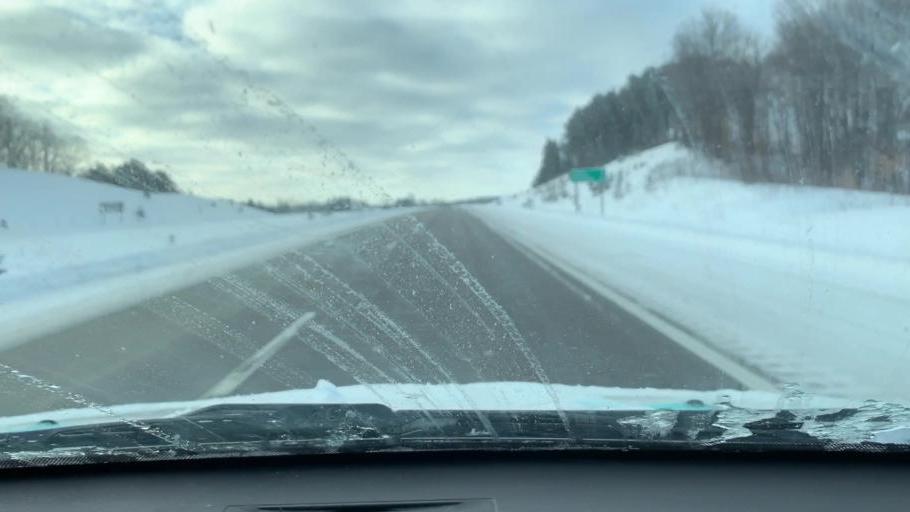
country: US
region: Michigan
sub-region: Wexford County
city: Manton
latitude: 44.3930
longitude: -85.3827
